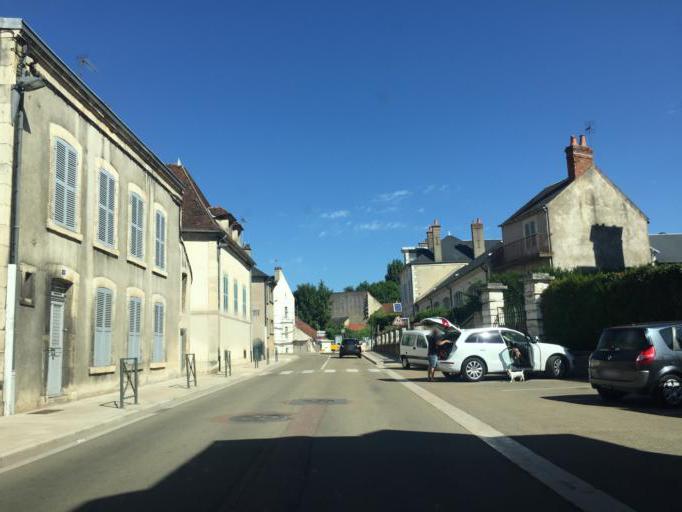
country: FR
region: Bourgogne
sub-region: Departement de la Nievre
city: Clamecy
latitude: 47.4606
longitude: 3.5223
